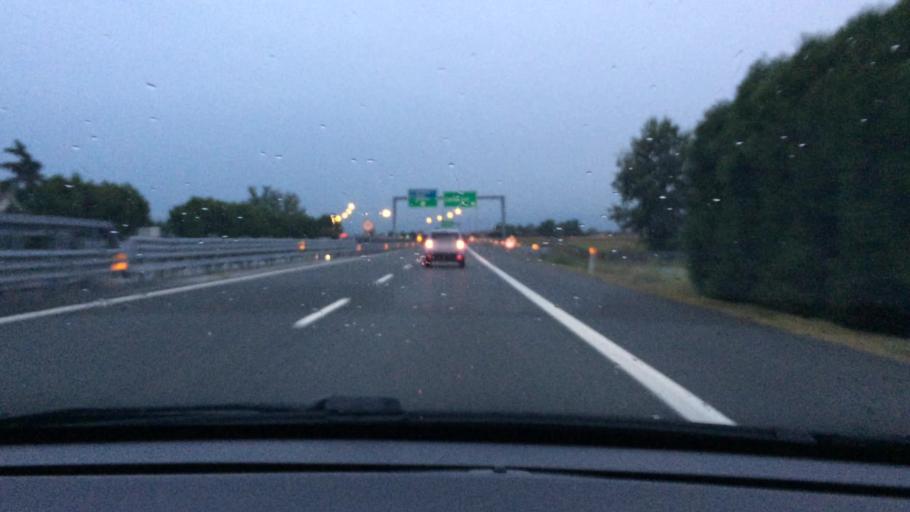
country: IT
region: Piedmont
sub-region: Provincia di Torino
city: Pasta
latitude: 44.9872
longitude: 7.5574
